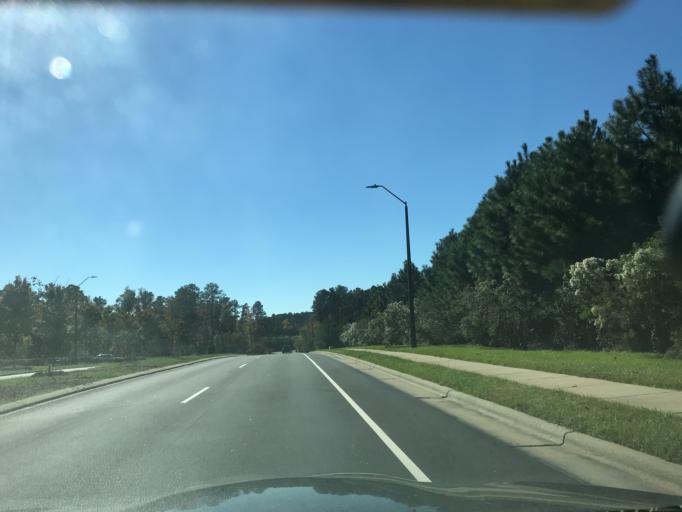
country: US
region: North Carolina
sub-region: Wake County
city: Morrisville
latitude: 35.9027
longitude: -78.7805
